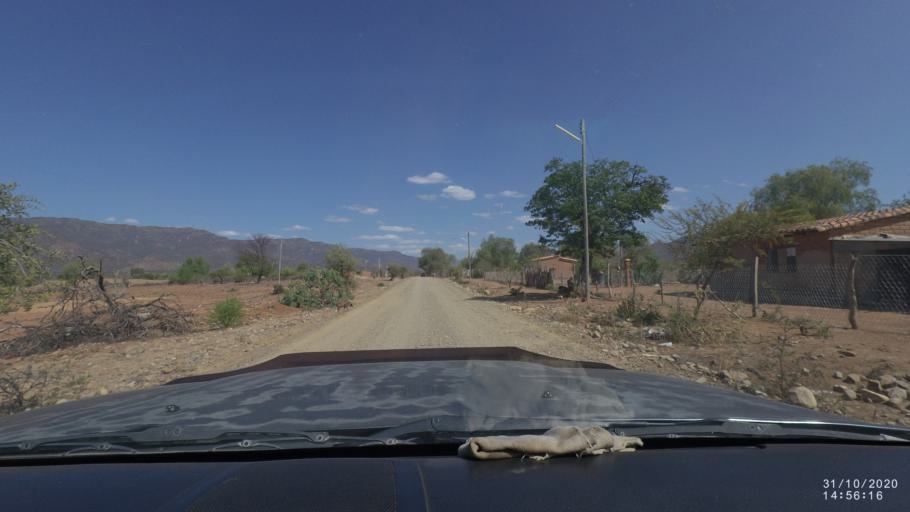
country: BO
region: Cochabamba
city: Aiquile
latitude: -18.2375
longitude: -64.8518
